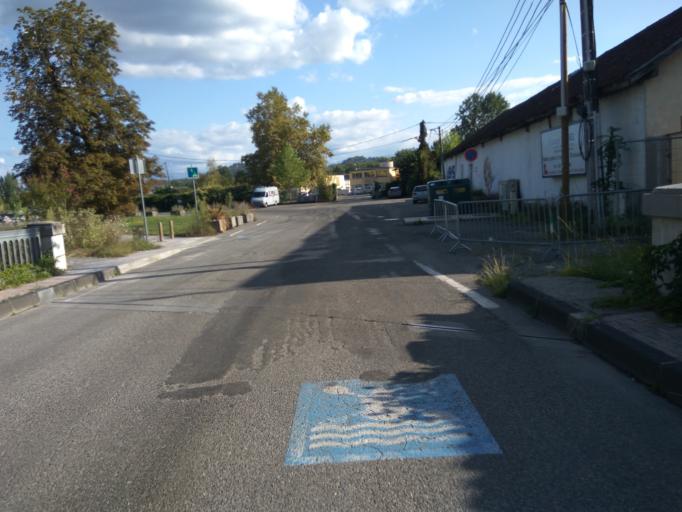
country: FR
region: Aquitaine
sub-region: Departement des Pyrenees-Atlantiques
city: Pau
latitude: 43.2922
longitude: -0.3636
